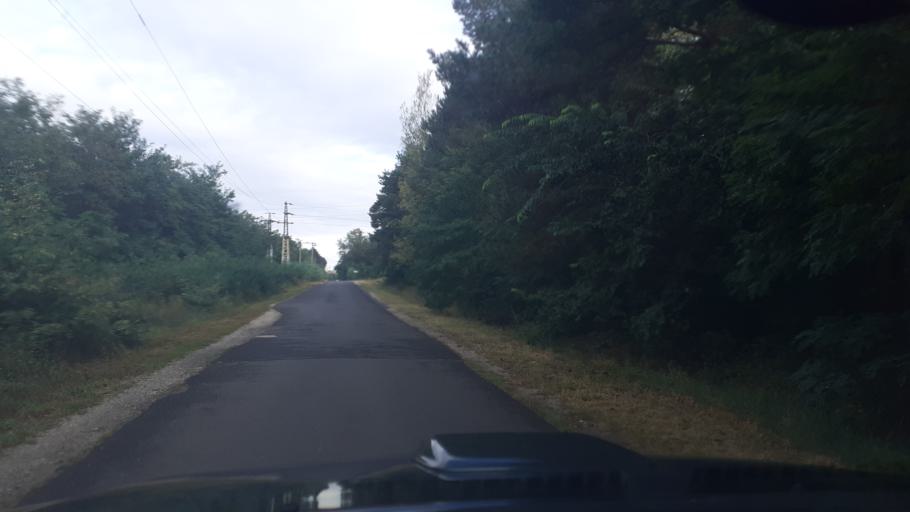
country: HU
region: Fejer
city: dunaujvaros
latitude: 46.9448
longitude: 18.8625
